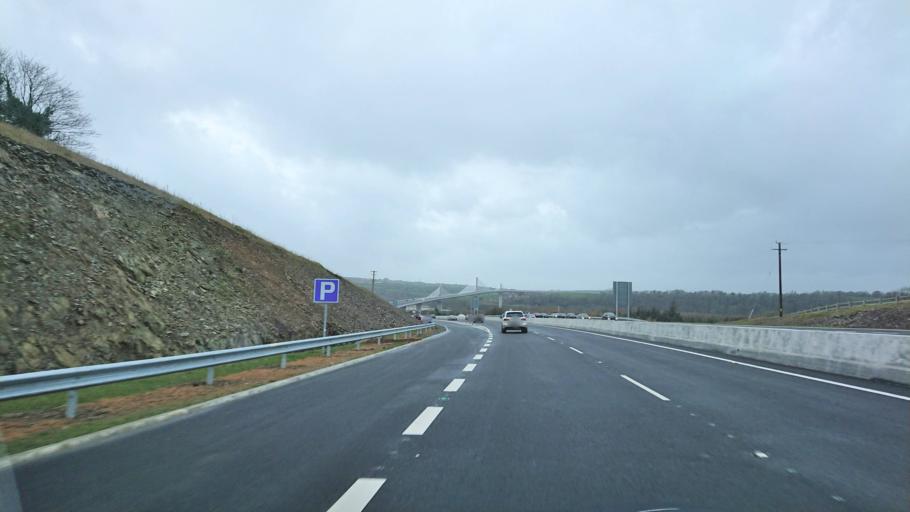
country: IE
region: Leinster
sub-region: Loch Garman
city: New Ross
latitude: 52.3601
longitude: -6.9770
